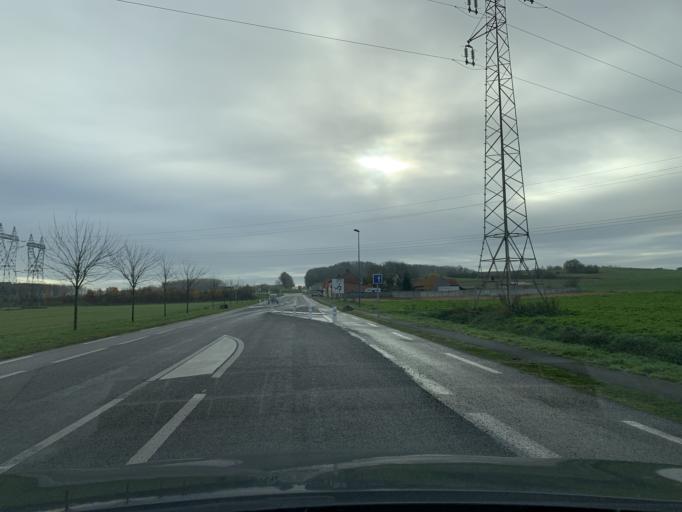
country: FR
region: Nord-Pas-de-Calais
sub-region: Departement du Nord
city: Cantin
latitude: 50.3071
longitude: 3.1305
